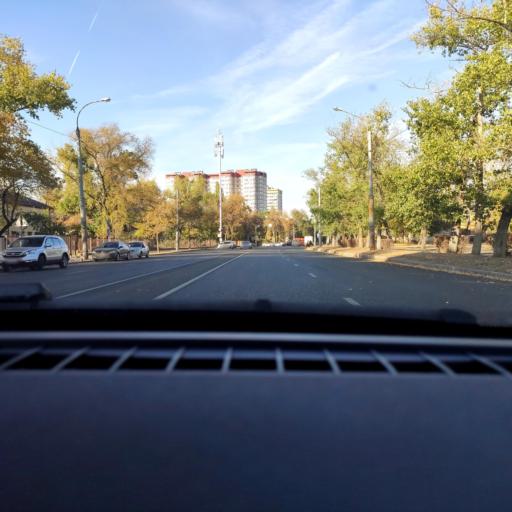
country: RU
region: Voronezj
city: Maslovka
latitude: 51.6137
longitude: 39.2468
